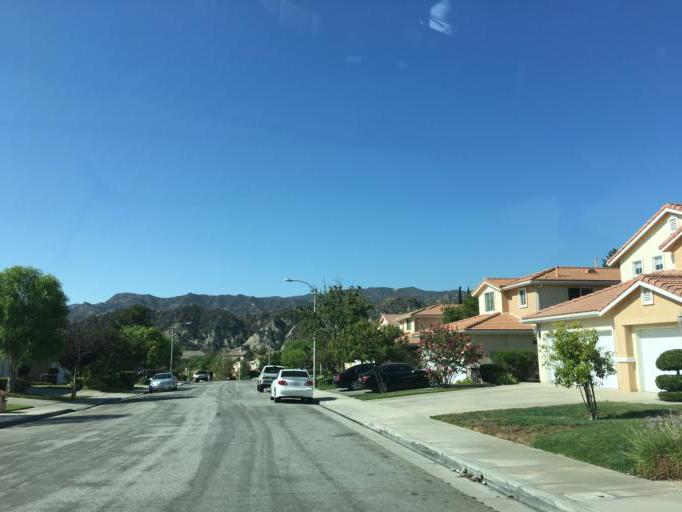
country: US
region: California
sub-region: Los Angeles County
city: Santa Clarita
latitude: 34.3904
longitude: -118.5907
